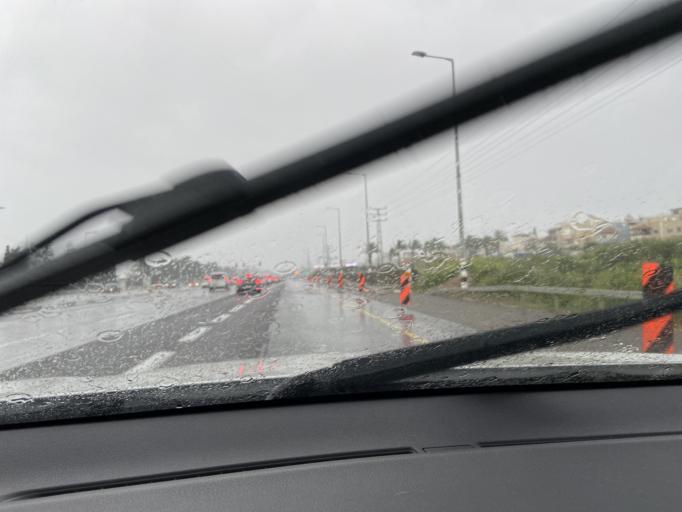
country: IL
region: Northern District
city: El Mazra`a
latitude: 32.9809
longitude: 35.0943
